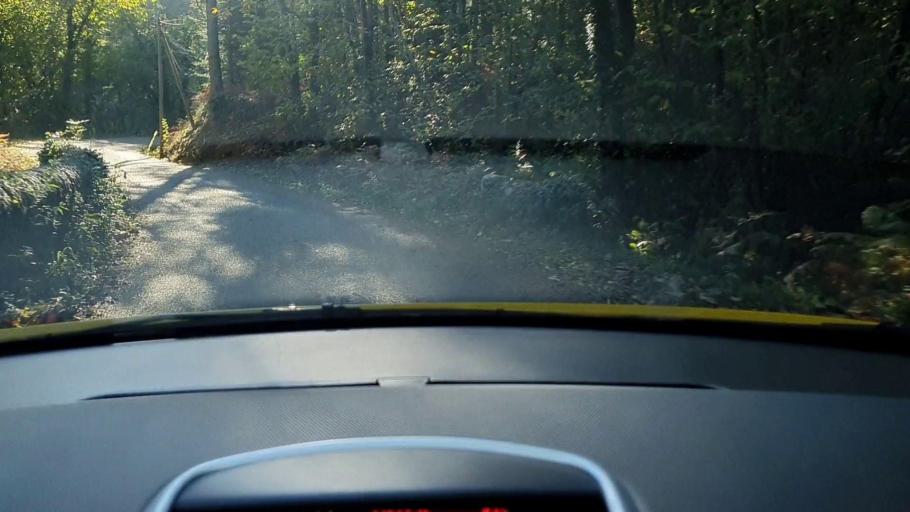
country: FR
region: Languedoc-Roussillon
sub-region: Departement du Gard
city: Sumene
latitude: 43.9821
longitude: 3.6798
